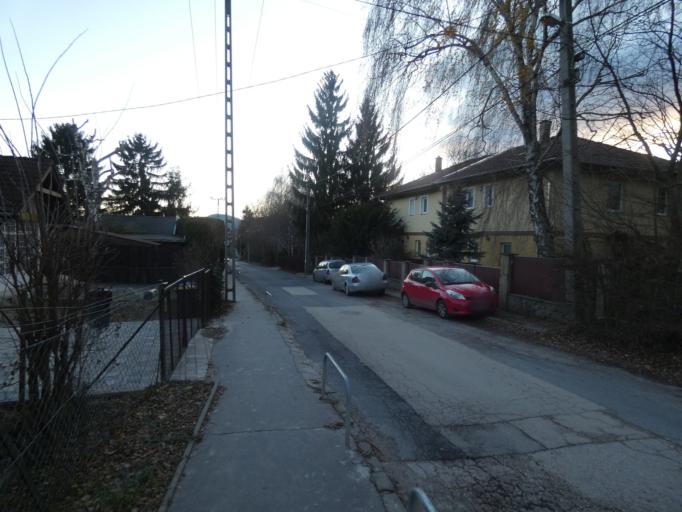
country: HU
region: Pest
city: Solymar
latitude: 47.5665
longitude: 18.9676
